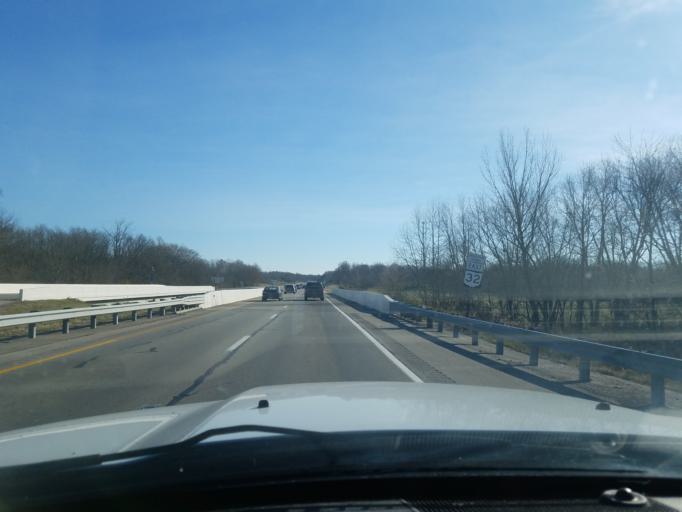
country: US
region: Ohio
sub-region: Brown County
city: Mount Orab
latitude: 39.0149
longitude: -83.8078
